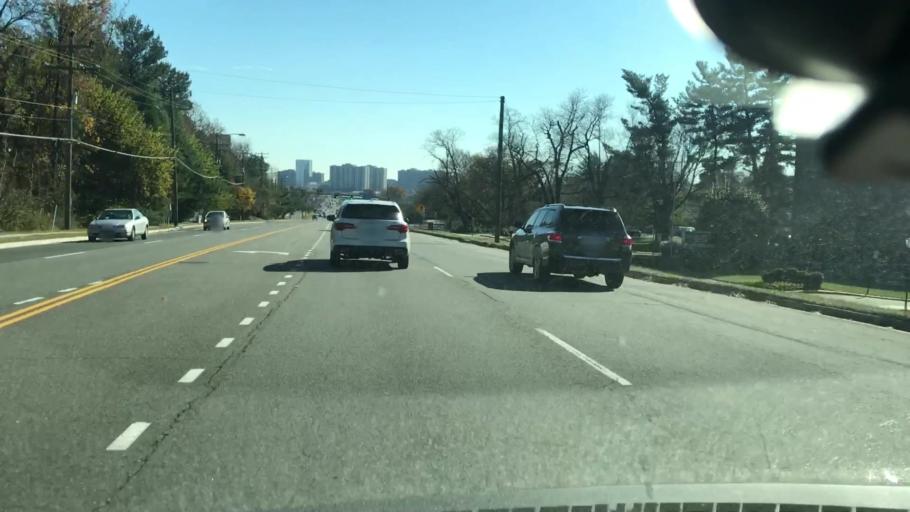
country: US
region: Virginia
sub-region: Fairfax County
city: Lake Barcroft
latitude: 38.8592
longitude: -77.1454
